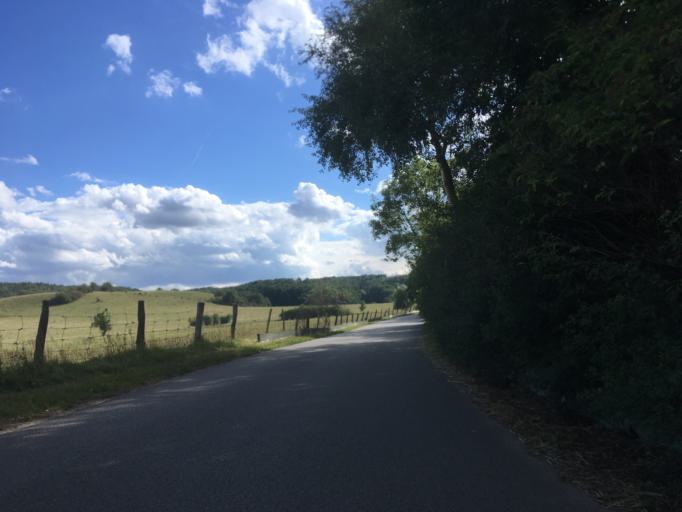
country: DE
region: Brandenburg
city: Oderberg
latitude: 52.9198
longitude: 14.0275
